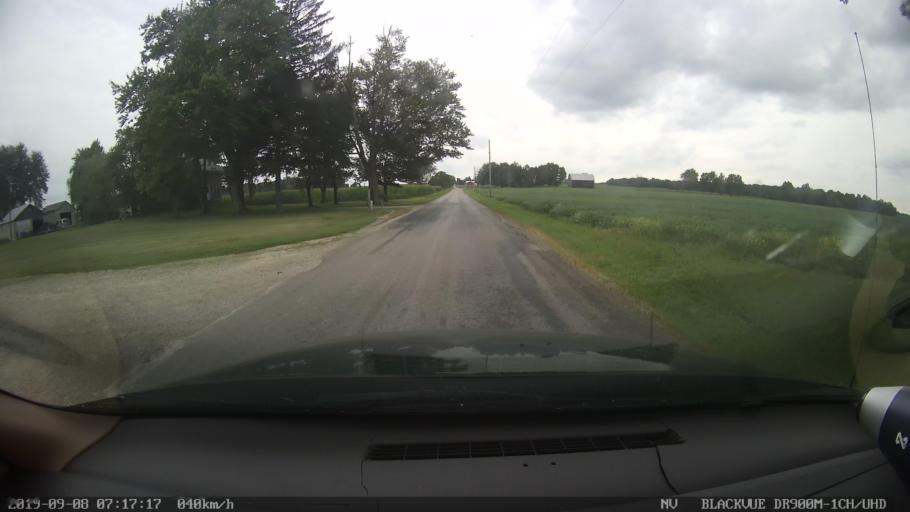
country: US
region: Ohio
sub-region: Richland County
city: Shelby
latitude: 40.9086
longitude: -82.7188
